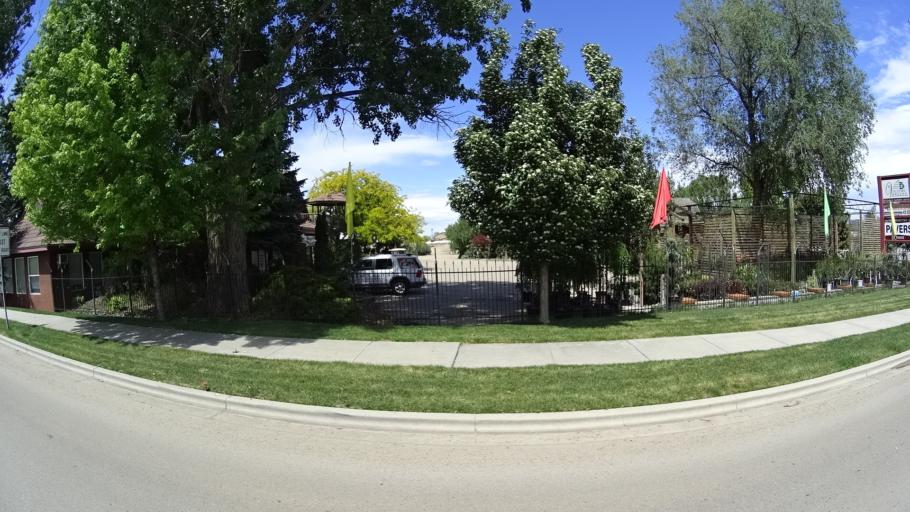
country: US
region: Idaho
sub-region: Ada County
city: Meridian
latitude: 43.5756
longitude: -116.3923
